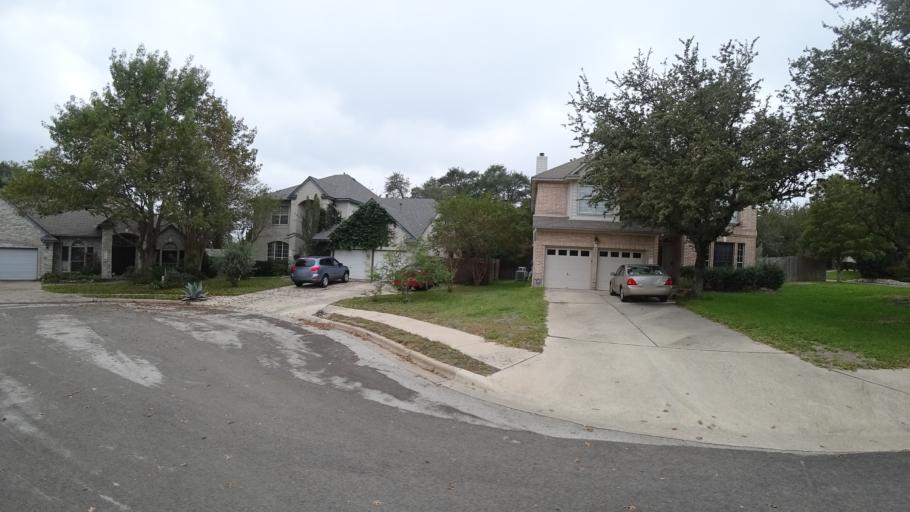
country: US
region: Texas
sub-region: Williamson County
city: Anderson Mill
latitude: 30.4341
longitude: -97.8199
